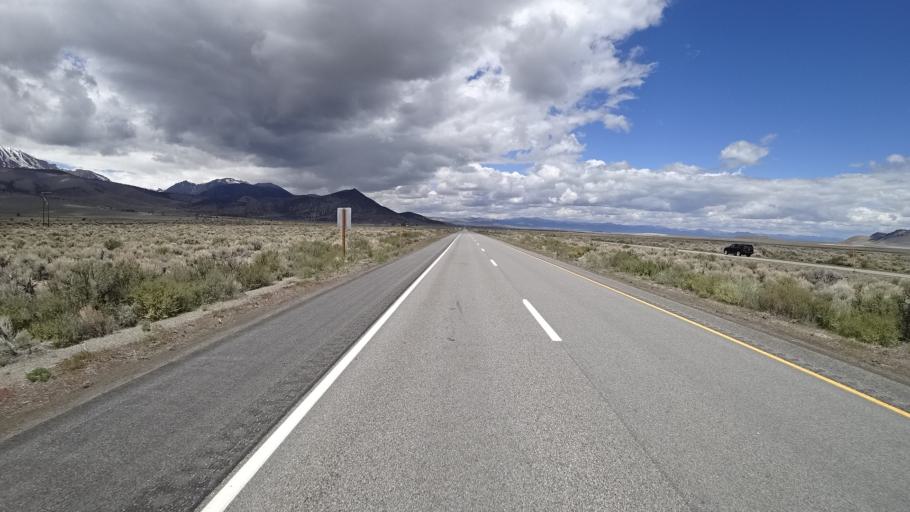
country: US
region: California
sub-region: Mono County
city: Mammoth Lakes
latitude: 37.8772
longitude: -119.0896
